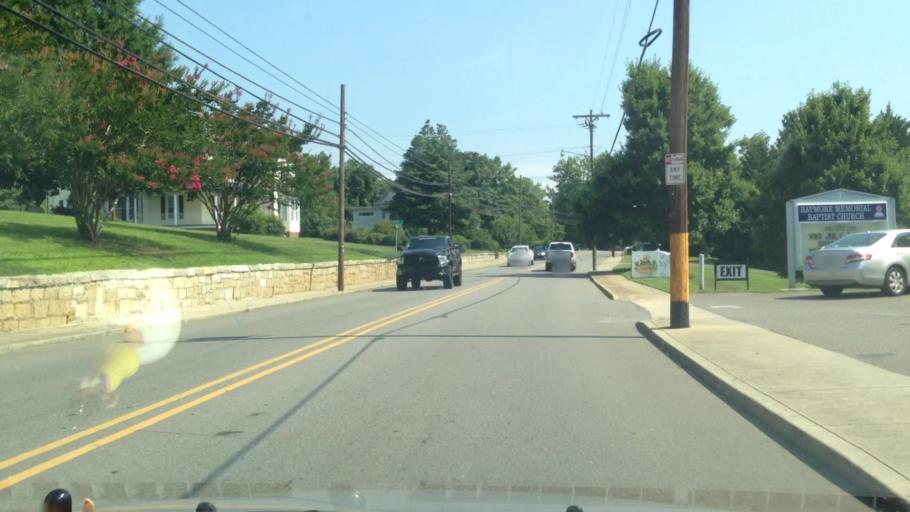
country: US
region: North Carolina
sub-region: Surry County
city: Mount Airy
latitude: 36.4956
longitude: -80.6096
